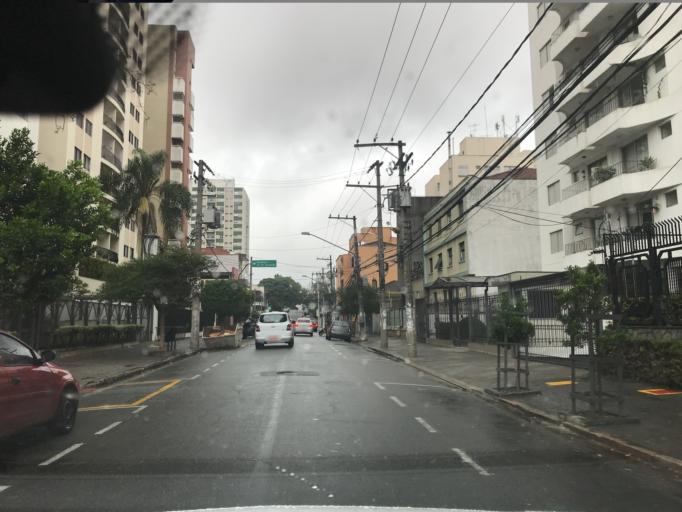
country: BR
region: Sao Paulo
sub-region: Sao Paulo
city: Sao Paulo
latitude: -23.5360
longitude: -46.6849
